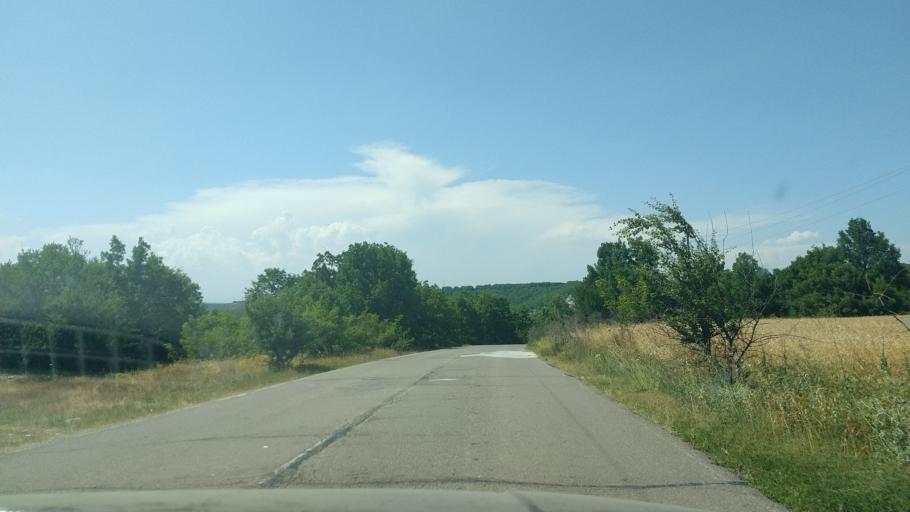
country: GR
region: West Macedonia
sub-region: Nomos Grevenon
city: Grevena
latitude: 40.0440
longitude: 21.4827
